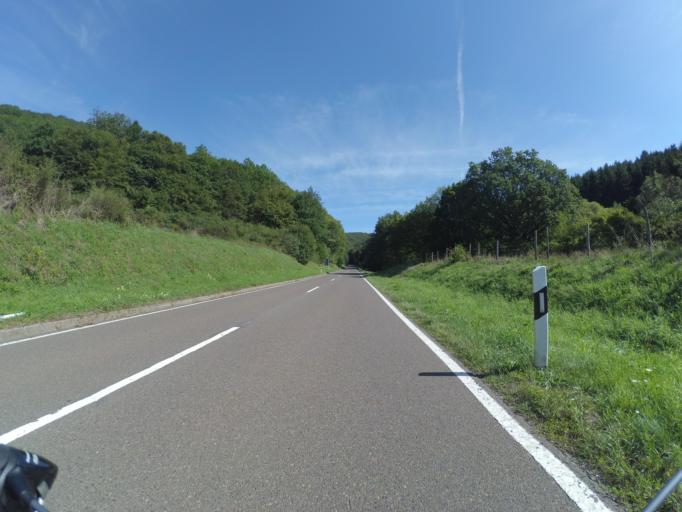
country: DE
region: Rheinland-Pfalz
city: Berglicht
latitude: 49.7988
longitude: 6.9761
